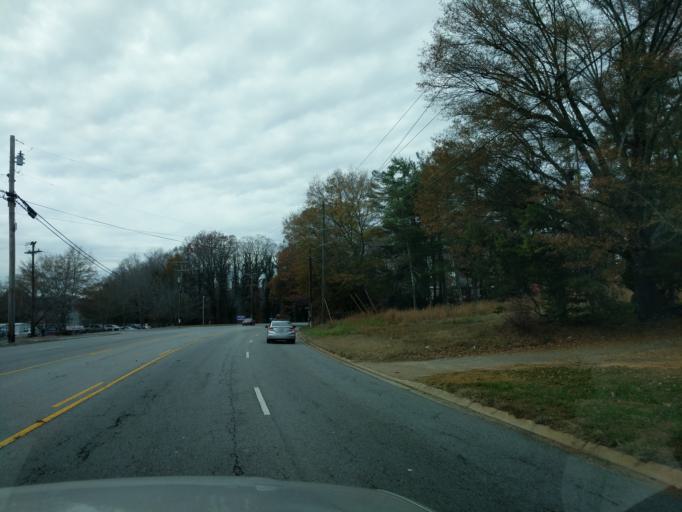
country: US
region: South Carolina
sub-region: Pickens County
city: Arial
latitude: 34.8365
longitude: -82.6235
